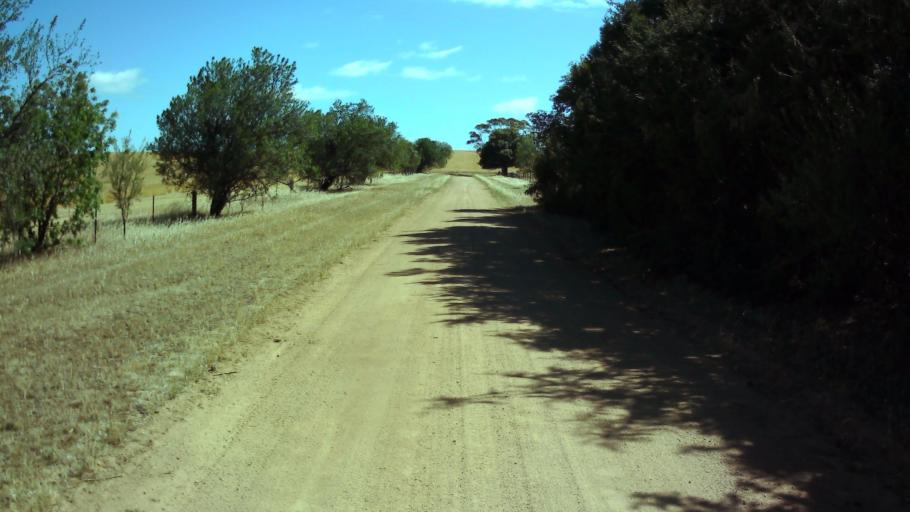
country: AU
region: New South Wales
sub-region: Weddin
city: Grenfell
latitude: -33.9666
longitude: 148.4108
